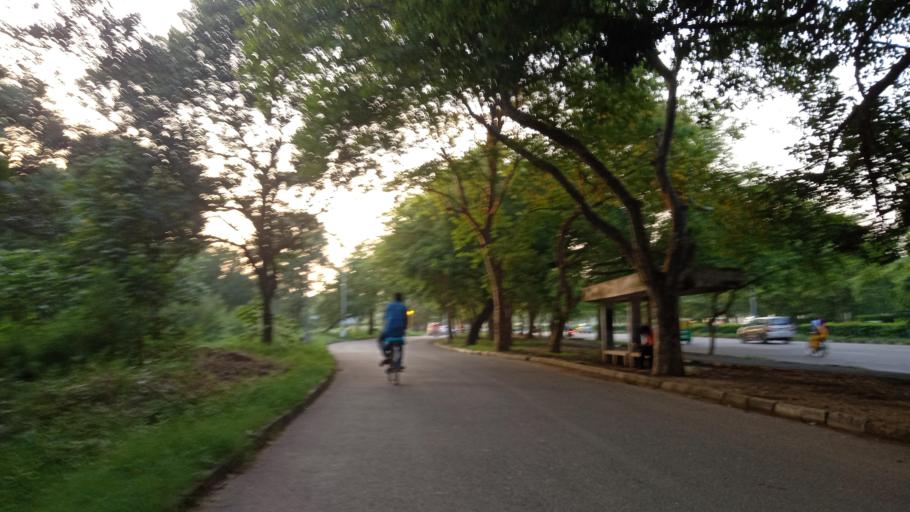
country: IN
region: Chandigarh
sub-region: Chandigarh
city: Chandigarh
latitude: 30.7471
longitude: 76.7518
